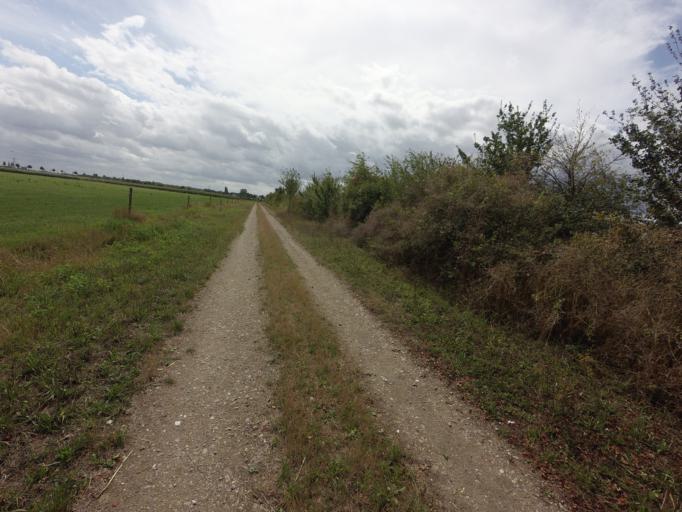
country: BE
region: Flanders
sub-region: Provincie Limburg
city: Maaseik
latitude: 51.1184
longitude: 5.8296
